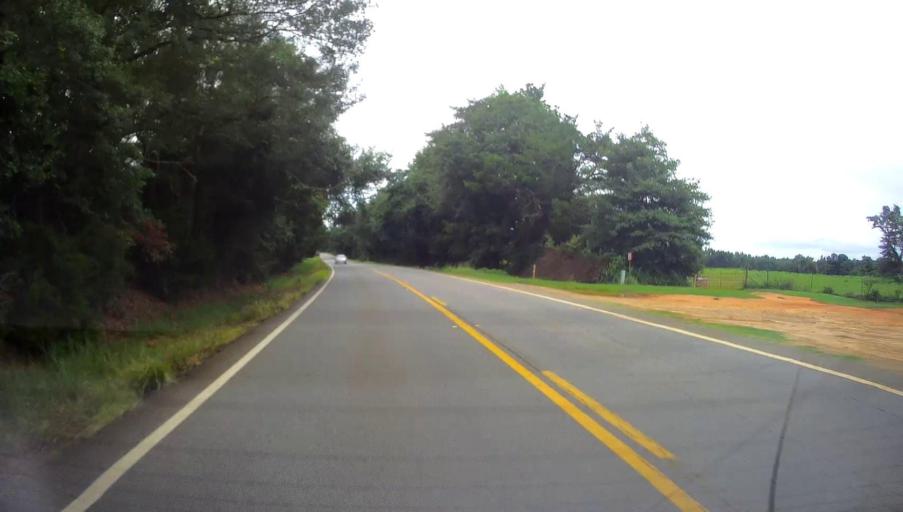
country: US
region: Georgia
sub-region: Marion County
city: Buena Vista
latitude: 32.2605
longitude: -84.4232
